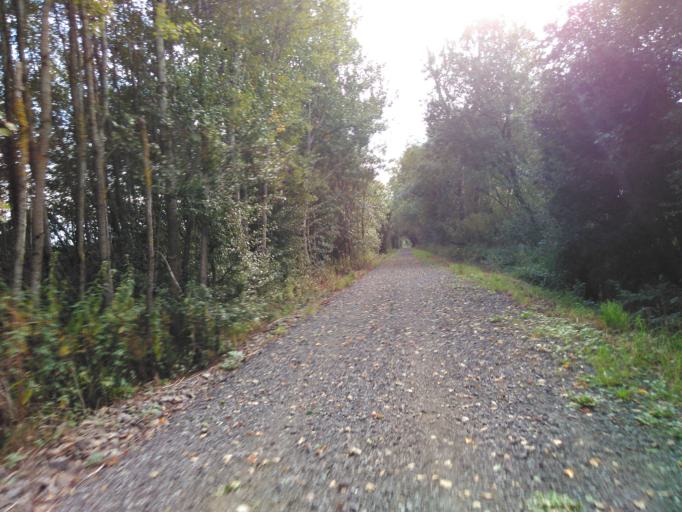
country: BE
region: Wallonia
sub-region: Province du Luxembourg
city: Neufchateau
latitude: 49.9162
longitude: 5.4261
